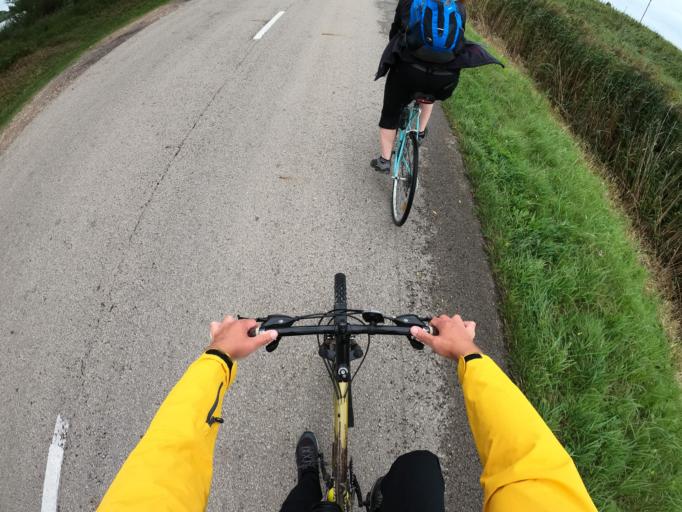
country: LT
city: Rusne
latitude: 55.3324
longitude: 21.3727
